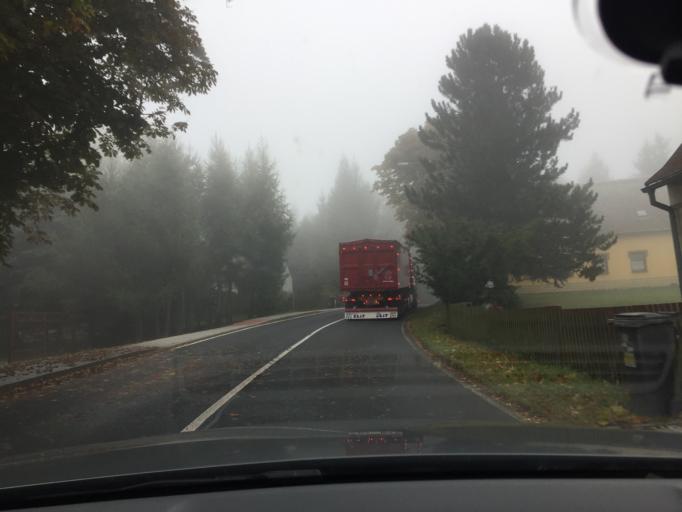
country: CZ
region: Ustecky
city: Libouchec
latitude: 50.7853
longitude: 14.0137
